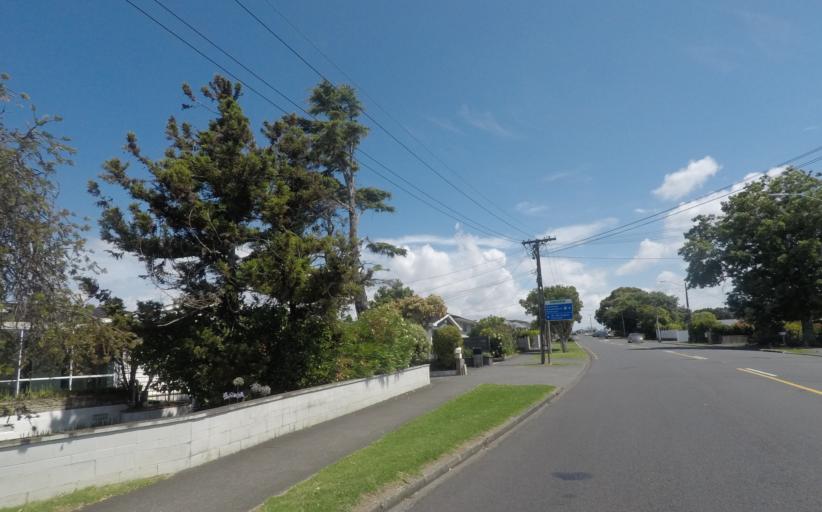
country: NZ
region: Auckland
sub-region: Auckland
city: Tamaki
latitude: -36.8726
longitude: 174.8436
